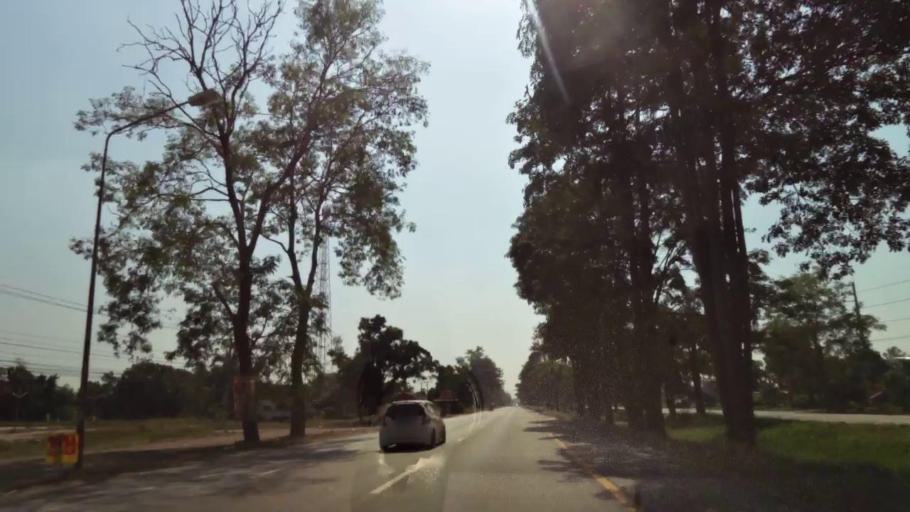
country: TH
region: Phichit
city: Wachira Barami
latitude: 16.6337
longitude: 100.1497
